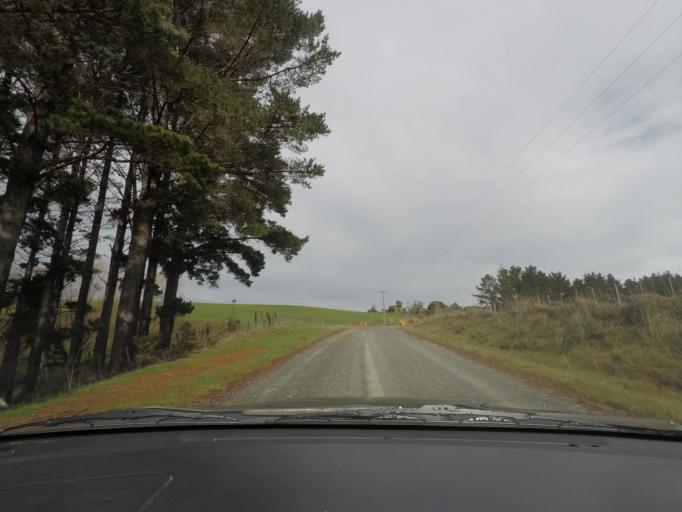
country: NZ
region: Auckland
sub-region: Auckland
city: Warkworth
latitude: -36.4532
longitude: 174.7507
